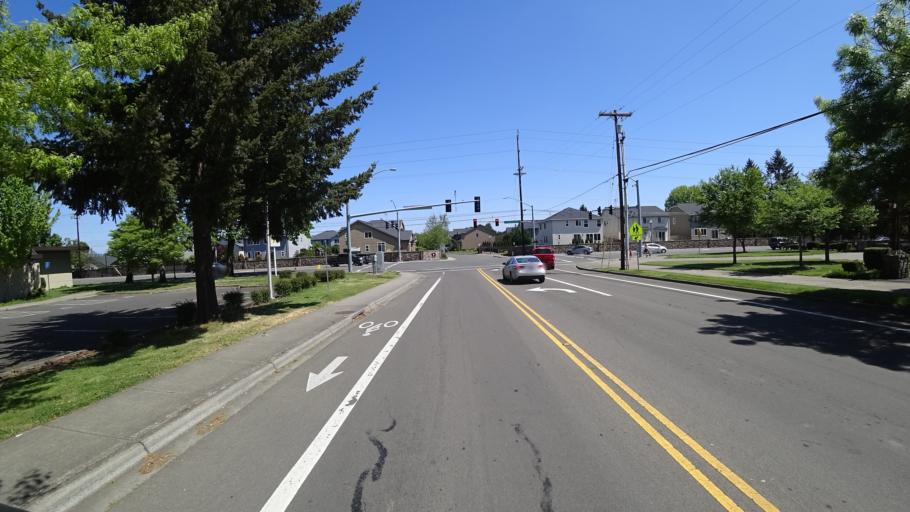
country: US
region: Oregon
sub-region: Washington County
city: Aloha
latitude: 45.5088
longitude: -122.9028
